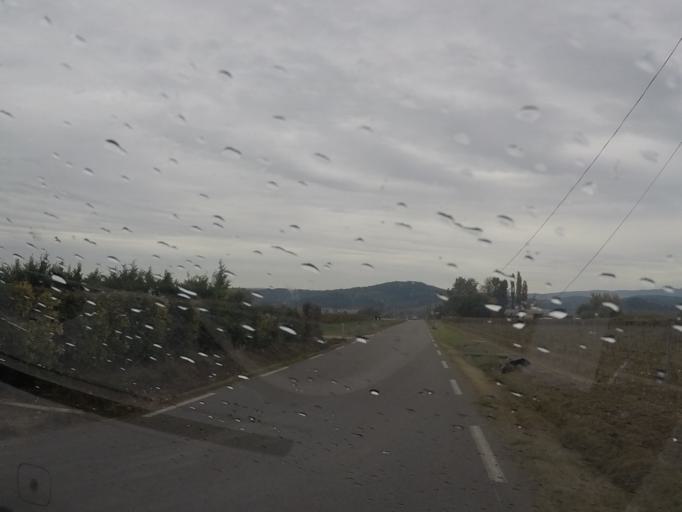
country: FR
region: Provence-Alpes-Cote d'Azur
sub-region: Departement du Vaucluse
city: Bonnieux
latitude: 43.8452
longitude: 5.2862
